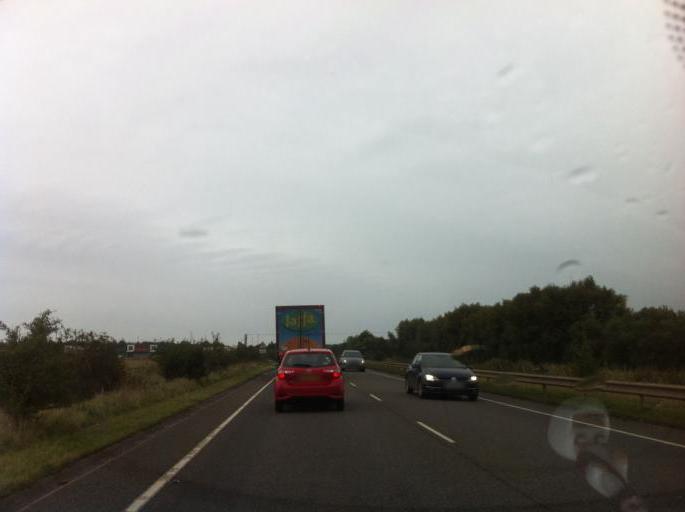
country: GB
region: England
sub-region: Lincolnshire
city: Kirton
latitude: 52.8861
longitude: -0.0869
